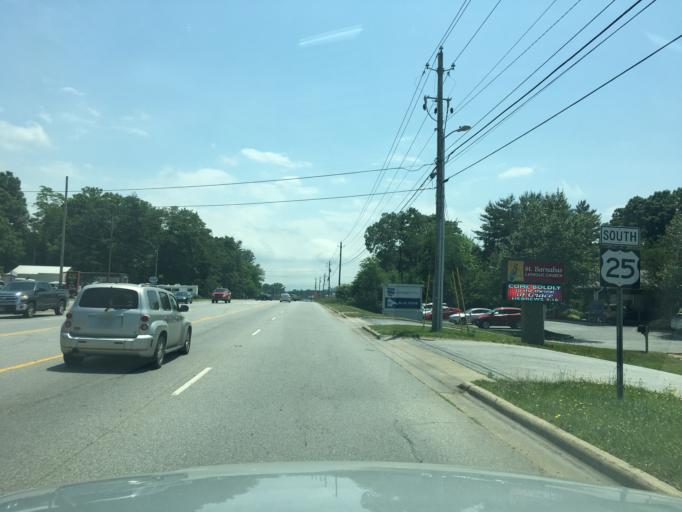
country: US
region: North Carolina
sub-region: Henderson County
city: Fletcher
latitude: 35.4517
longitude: -82.5099
